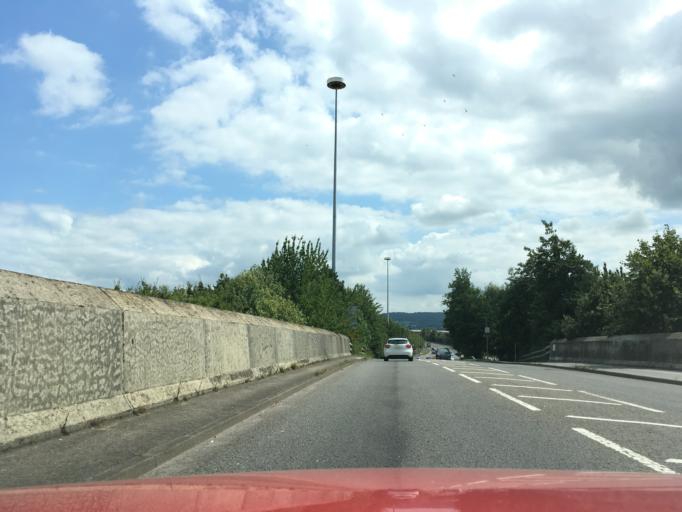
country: GB
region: England
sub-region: Gloucestershire
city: Gloucester
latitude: 51.8592
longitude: -2.2231
